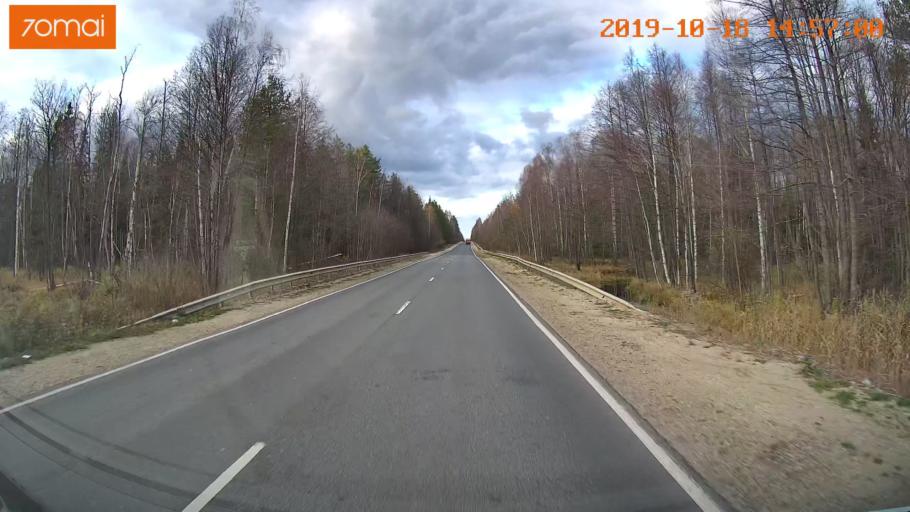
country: RU
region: Vladimir
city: Kurlovo
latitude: 55.4730
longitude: 40.5840
